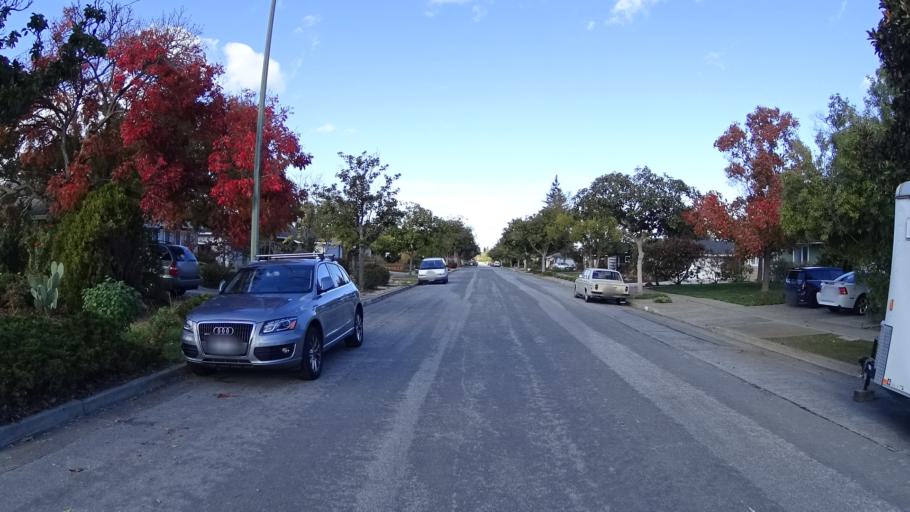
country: US
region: California
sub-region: Santa Clara County
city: Cupertino
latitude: 37.3423
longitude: -122.0511
